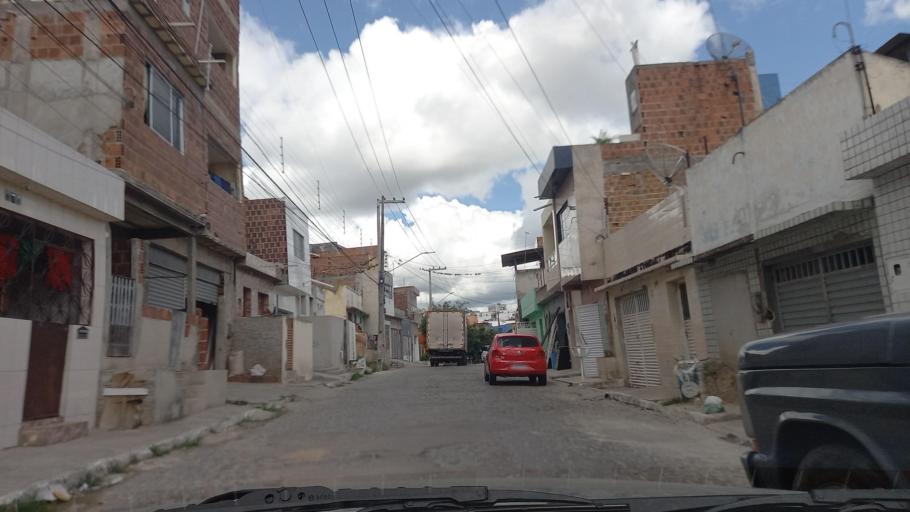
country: BR
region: Pernambuco
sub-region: Caruaru
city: Caruaru
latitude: -8.2979
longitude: -35.9710
